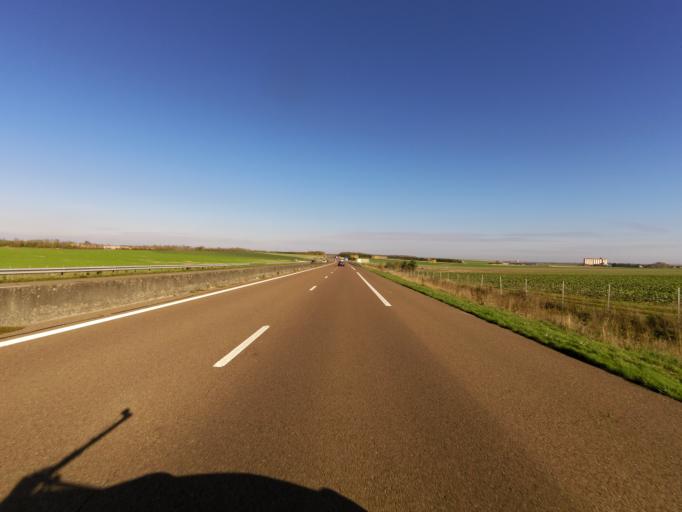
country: FR
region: Champagne-Ardenne
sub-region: Departement de la Marne
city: Compertrix
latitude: 48.8682
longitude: 4.2876
